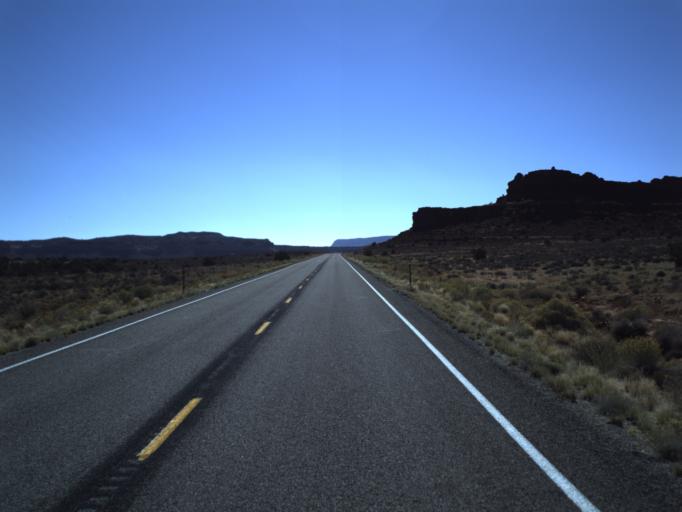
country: US
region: Utah
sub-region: San Juan County
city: Blanding
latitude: 37.7891
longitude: -110.2979
